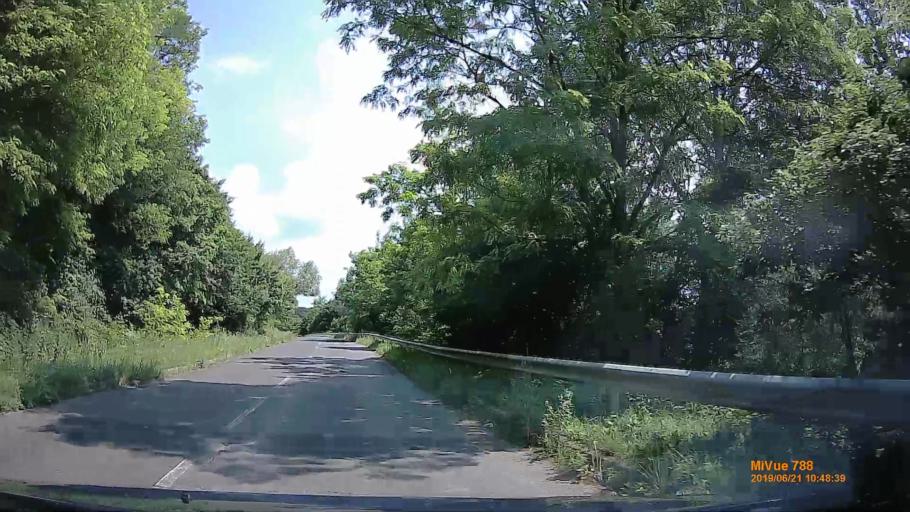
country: HU
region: Baranya
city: Buekkoesd
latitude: 46.1243
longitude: 18.0288
